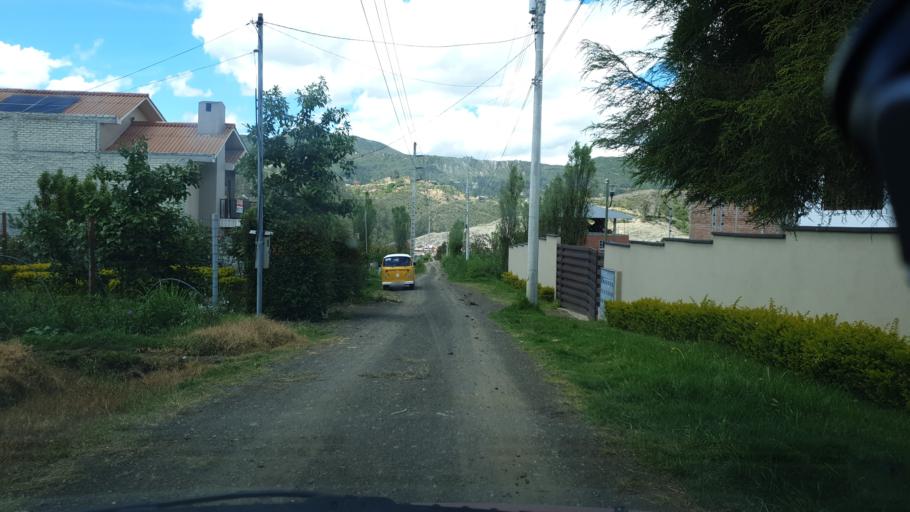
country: EC
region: Azuay
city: Cuenca
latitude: -2.8735
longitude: -78.9503
